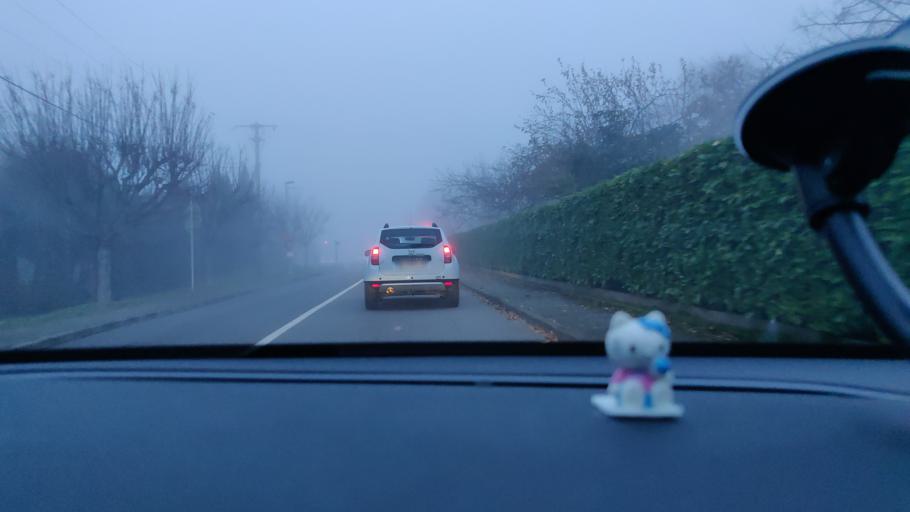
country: FR
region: Midi-Pyrenees
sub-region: Departement de la Haute-Garonne
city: Vieille-Toulouse
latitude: 43.5060
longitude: 1.4594
